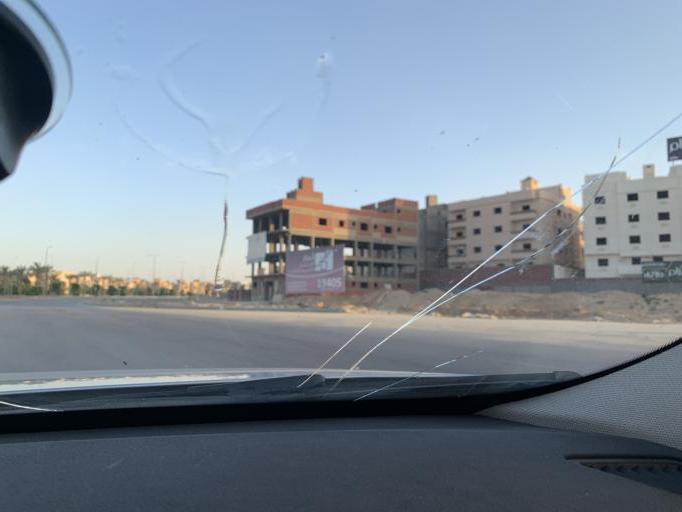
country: EG
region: Muhafazat al Qalyubiyah
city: Al Khankah
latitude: 30.0266
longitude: 31.5283
